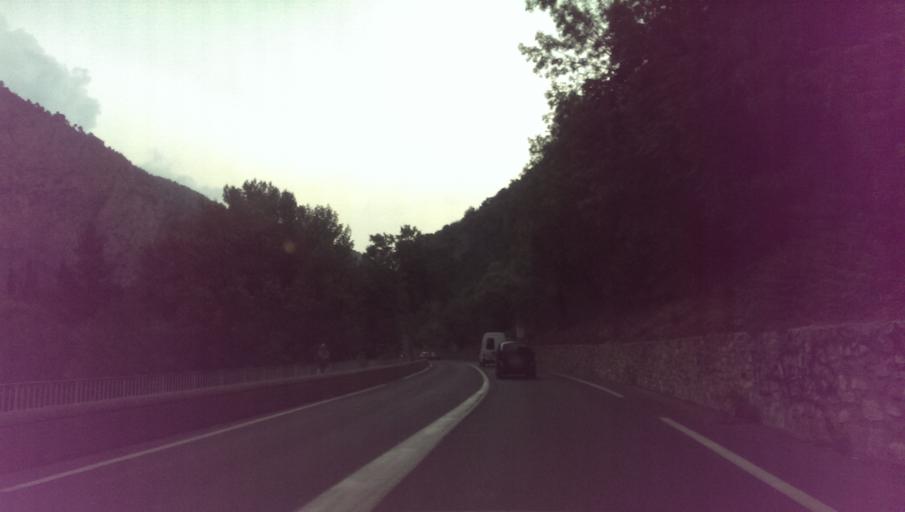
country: FR
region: Languedoc-Roussillon
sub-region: Departement des Pyrenees-Orientales
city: Ria-Sirach
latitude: 42.5880
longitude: 2.3705
